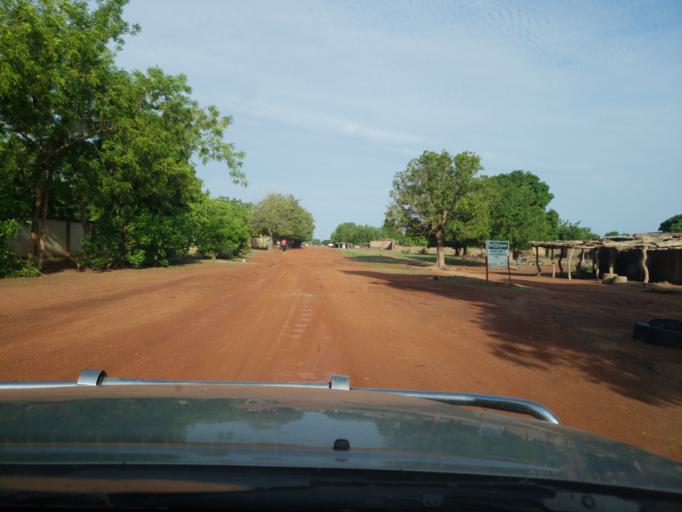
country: ML
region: Sikasso
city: Koutiala
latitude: 12.4227
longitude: -5.6834
